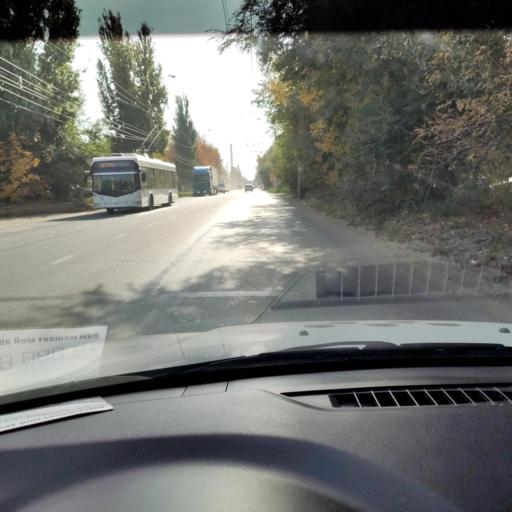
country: RU
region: Samara
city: Tol'yatti
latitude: 53.5660
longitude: 49.4569
